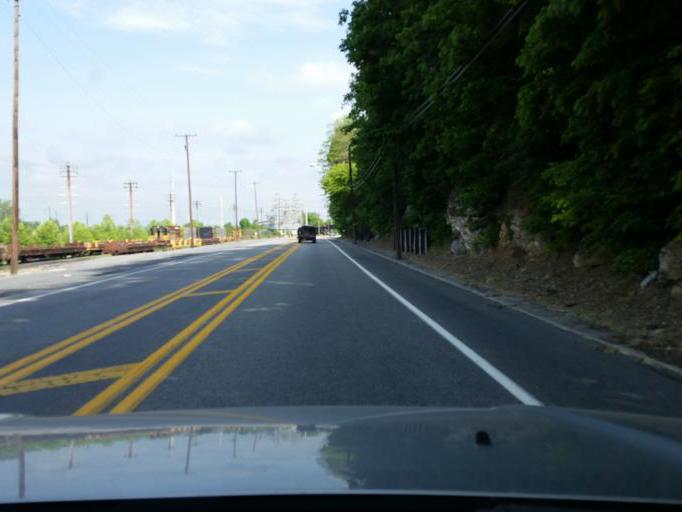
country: US
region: Pennsylvania
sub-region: Dauphin County
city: Bressler
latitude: 40.2192
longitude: -76.8205
